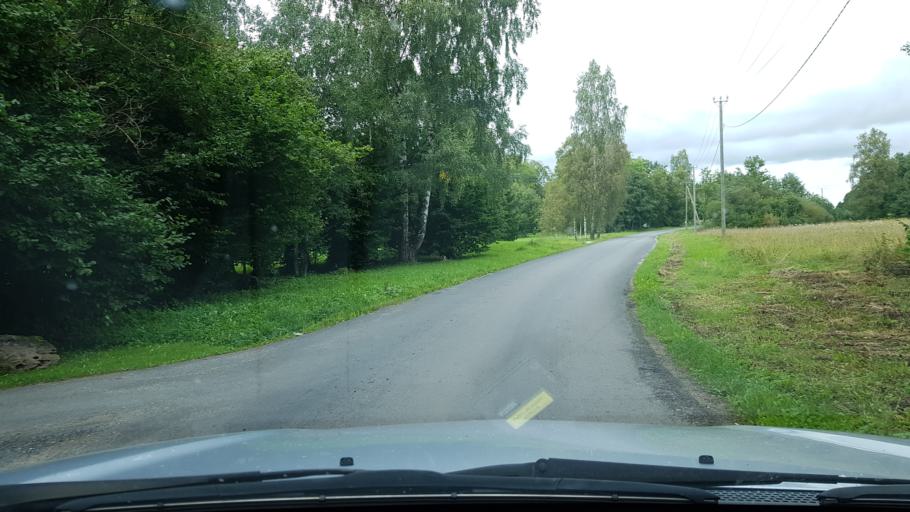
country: EE
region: Harju
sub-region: Rae vald
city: Vaida
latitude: 59.3465
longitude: 24.9600
